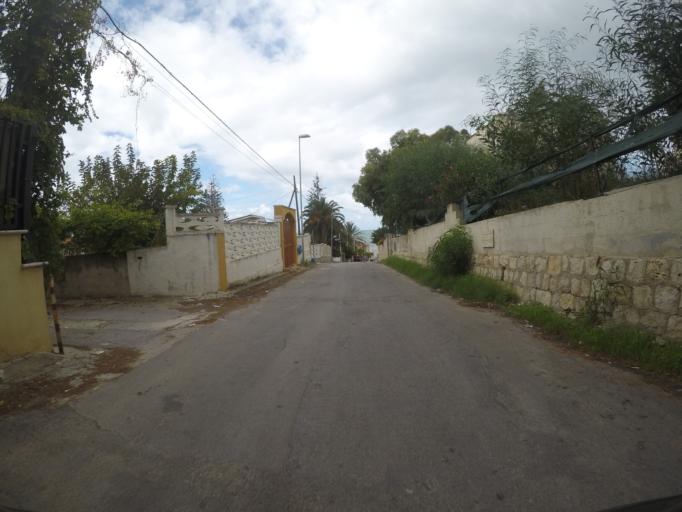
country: IT
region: Sicily
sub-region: Palermo
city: Trappeto
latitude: 38.0713
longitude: 13.0553
